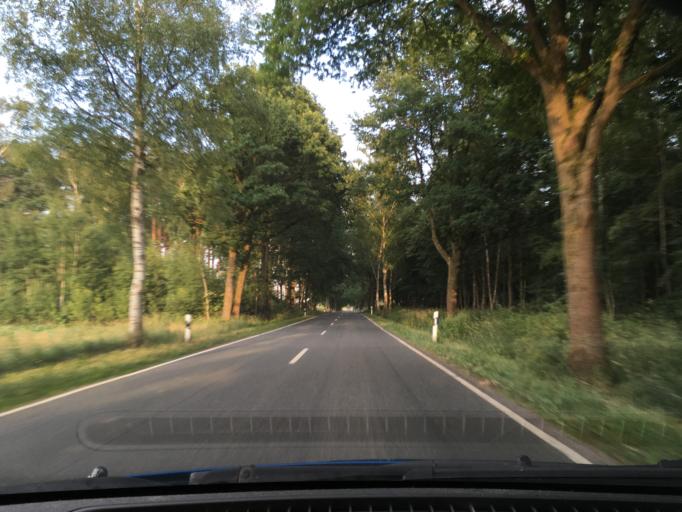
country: DE
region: Lower Saxony
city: Scharnhorst
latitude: 52.7236
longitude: 10.2919
